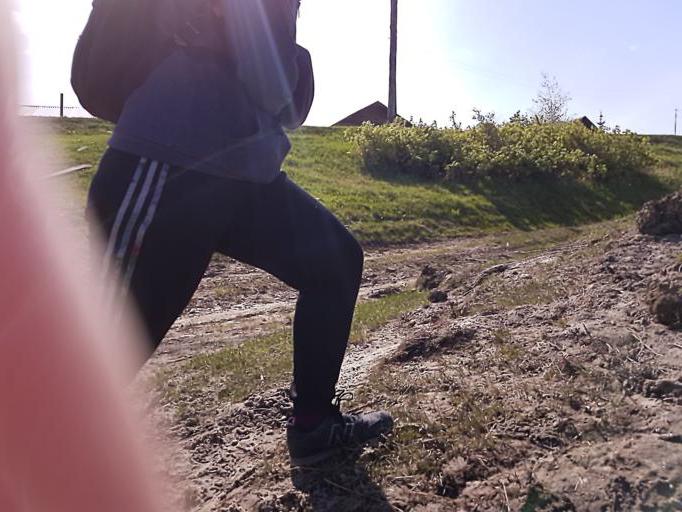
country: RU
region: Sakha
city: Tabaga
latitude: 61.8248
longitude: 129.6317
